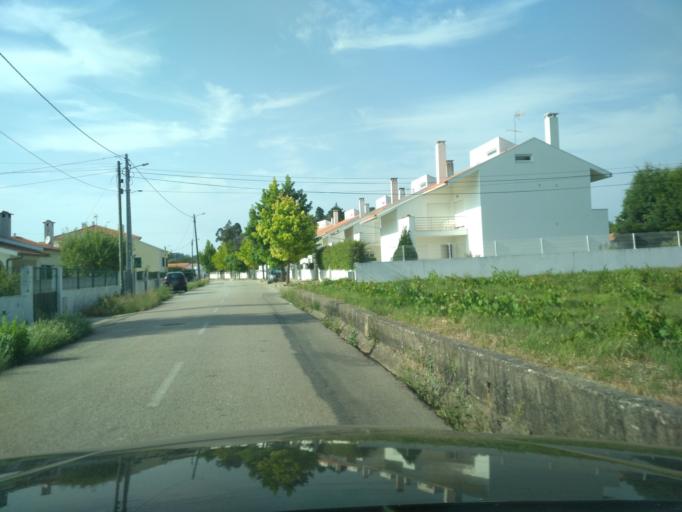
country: PT
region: Coimbra
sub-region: Condeixa-A-Nova
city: Condeixa-a-Nova
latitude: 40.1350
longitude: -8.4676
